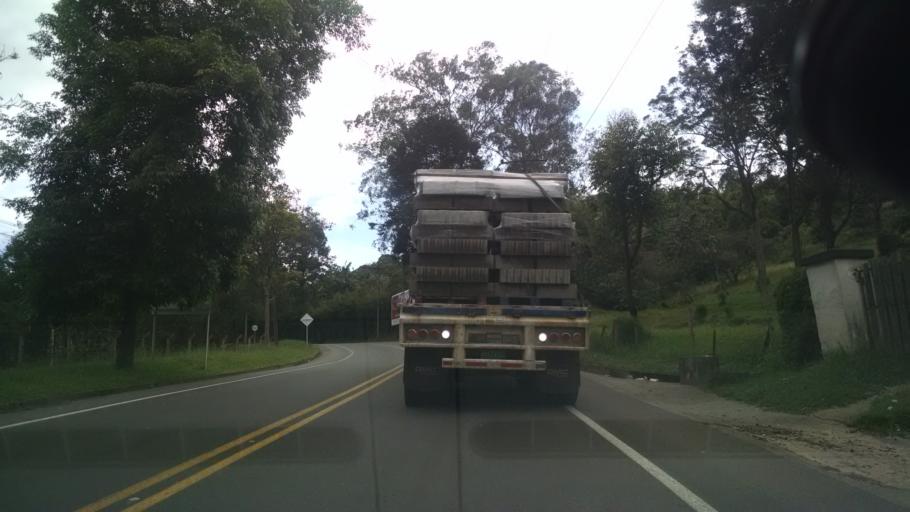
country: CO
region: Antioquia
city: Caldas
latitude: 6.0533
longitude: -75.6296
